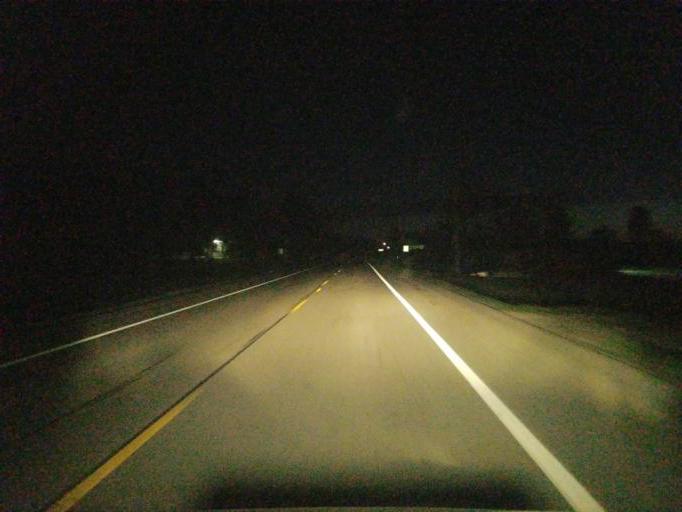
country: US
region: Ohio
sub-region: Geauga County
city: Middlefield
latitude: 41.5002
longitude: -81.0514
